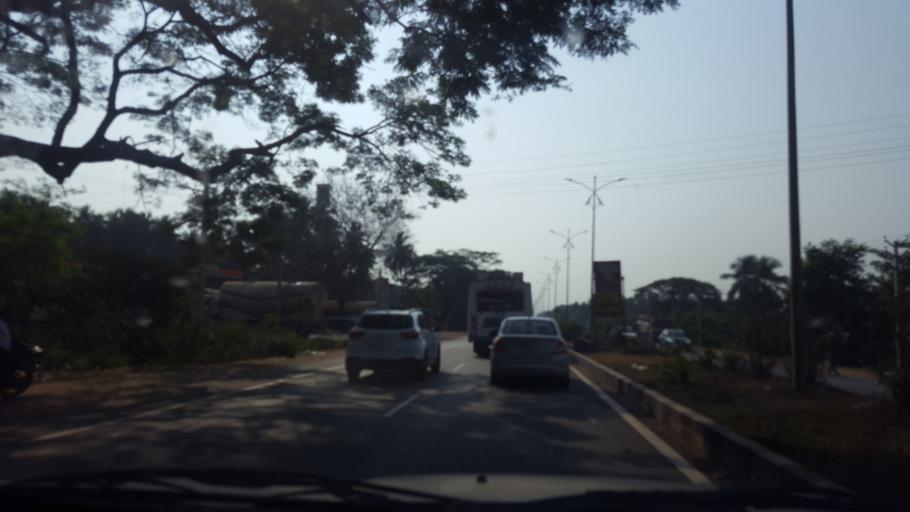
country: IN
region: Andhra Pradesh
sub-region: Vishakhapatnam
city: Anakapalle
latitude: 17.6763
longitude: 83.0179
